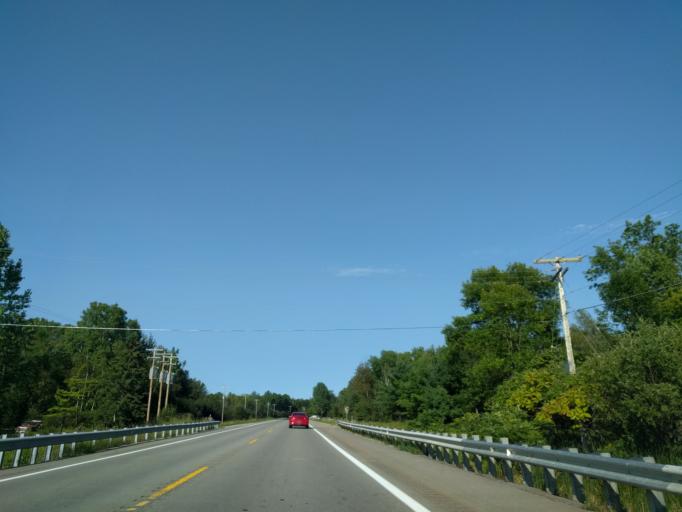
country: US
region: Michigan
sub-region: Menominee County
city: Menominee
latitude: 45.1816
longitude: -87.5668
